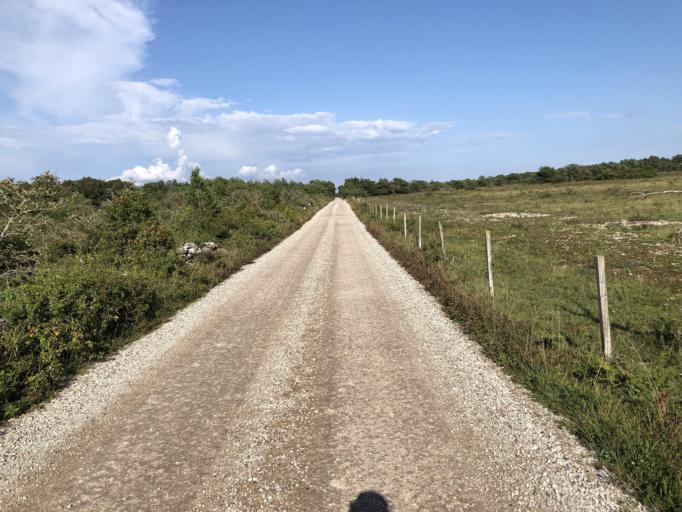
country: SE
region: Gotland
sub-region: Gotland
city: Hemse
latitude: 57.0311
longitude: 18.2203
